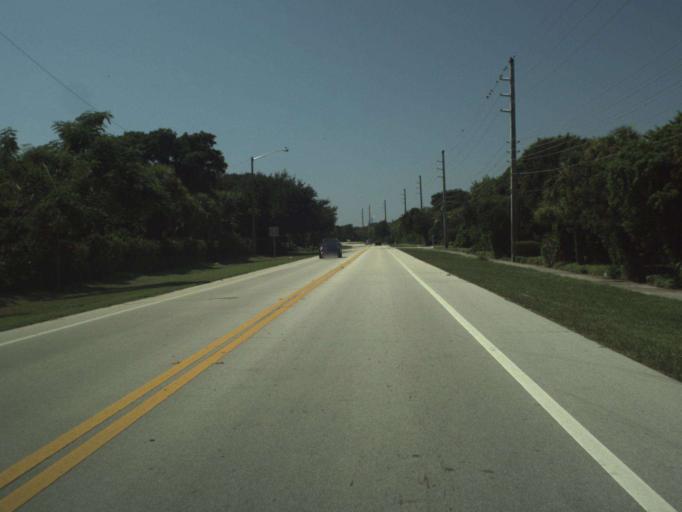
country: US
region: Florida
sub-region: Indian River County
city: South Beach
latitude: 27.6200
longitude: -80.3508
